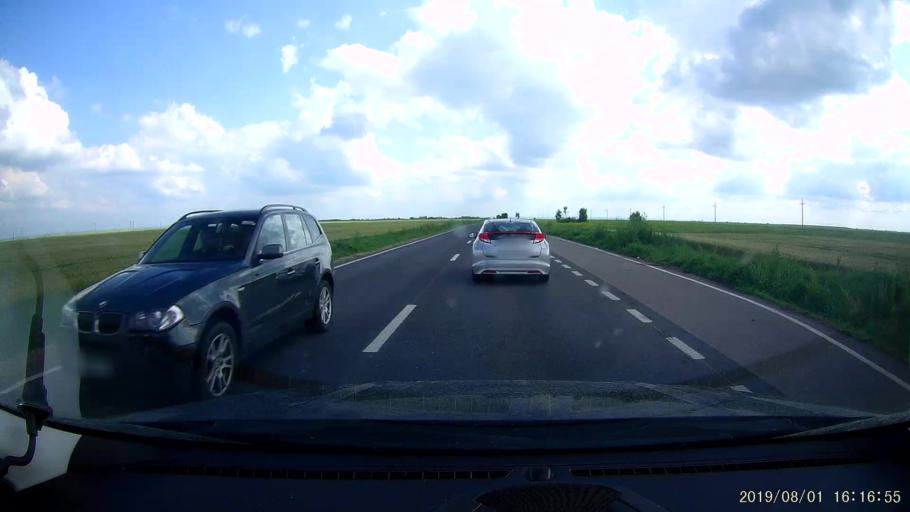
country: RO
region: Calarasi
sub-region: Comuna Stefan Voda
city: Stefan Voda
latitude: 44.3124
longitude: 27.3566
